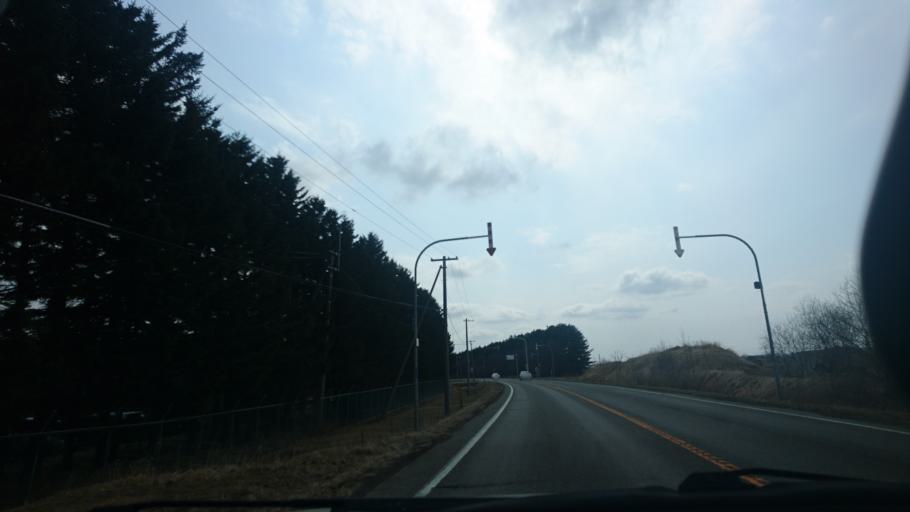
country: JP
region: Hokkaido
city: Otofuke
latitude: 43.1606
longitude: 143.2475
